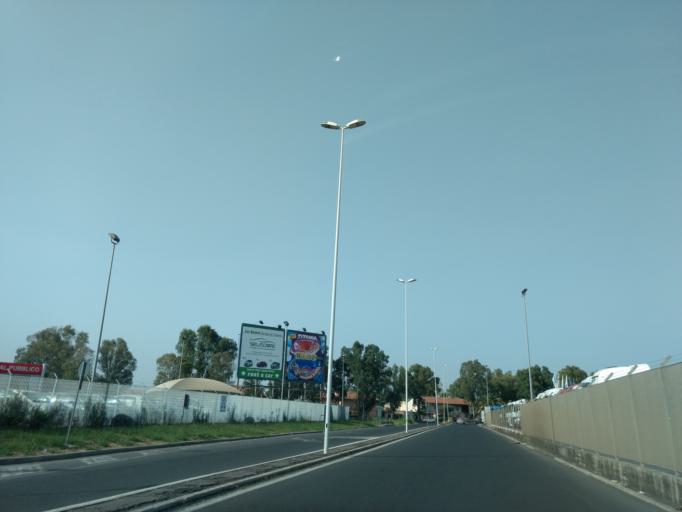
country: IT
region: Sicily
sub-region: Catania
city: Catania
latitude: 37.4730
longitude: 15.0711
